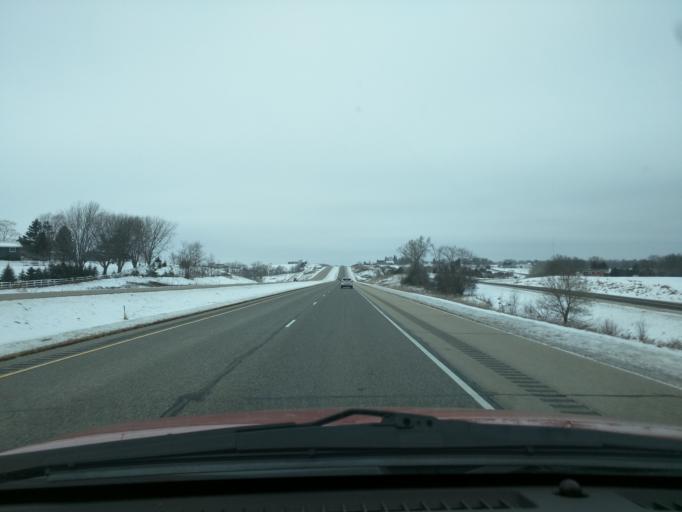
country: US
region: Minnesota
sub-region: Winona County
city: Winona
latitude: 43.9439
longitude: -91.6372
